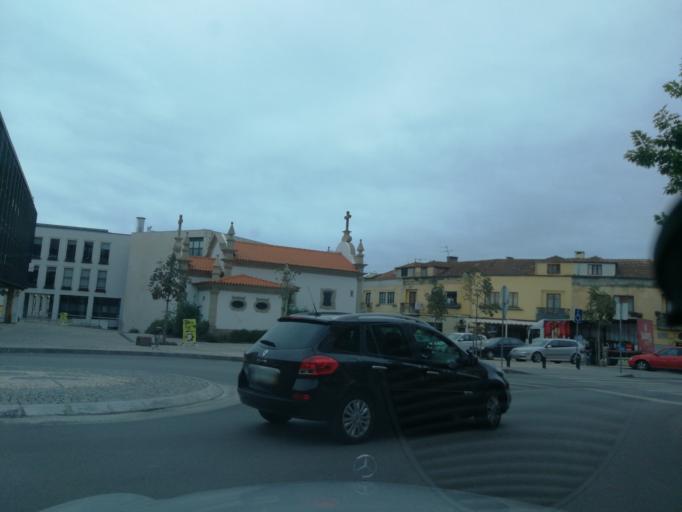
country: PT
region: Aveiro
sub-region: Agueda
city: Agueda
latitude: 40.5764
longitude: -8.4469
